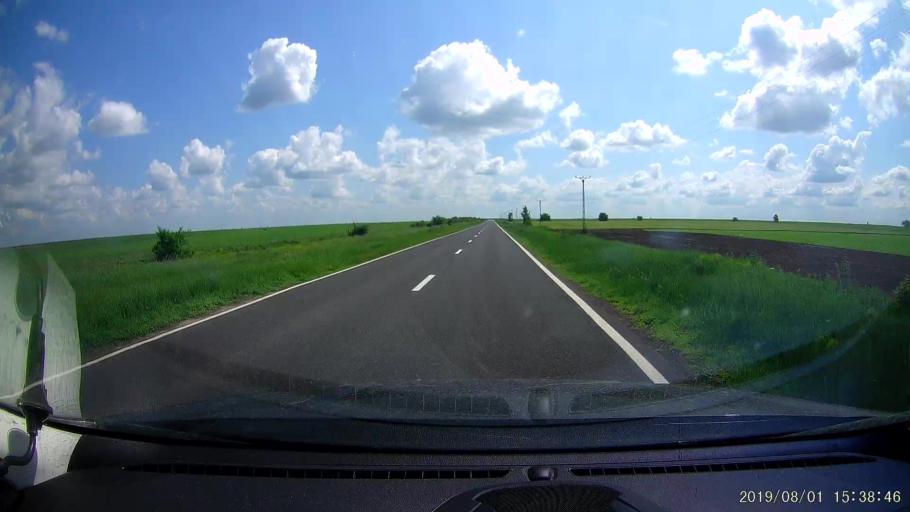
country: RO
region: Braila
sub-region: Comuna Insuratei
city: Insuratei
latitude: 44.8735
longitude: 27.5712
